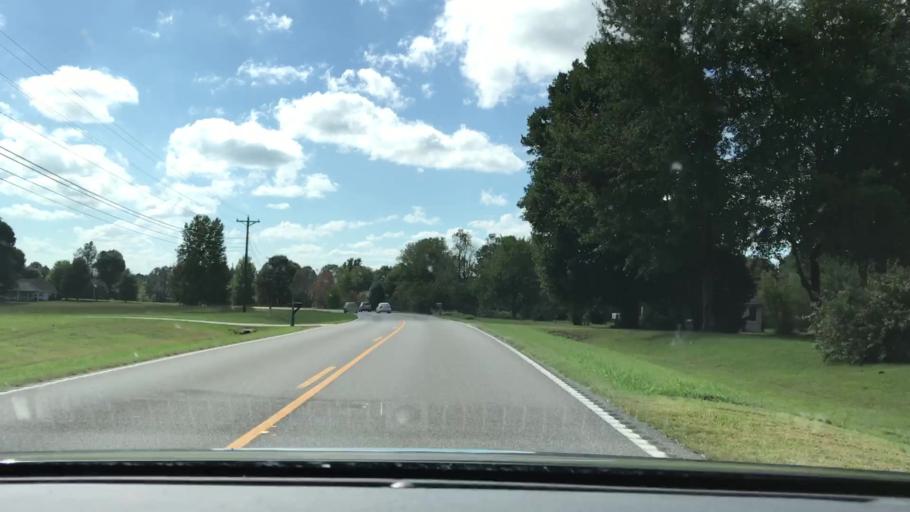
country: US
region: Kentucky
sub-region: McCracken County
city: Reidland
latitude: 36.9825
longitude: -88.5160
